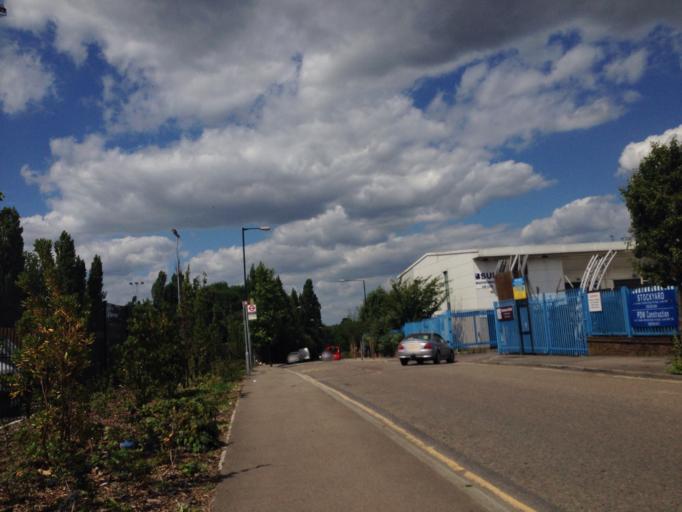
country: GB
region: England
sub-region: Greater London
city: Acton
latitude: 51.5329
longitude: -0.2780
